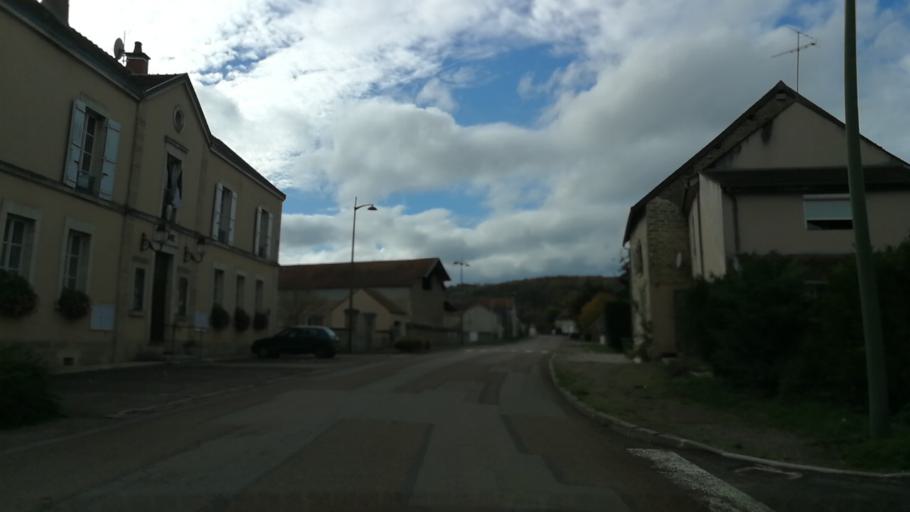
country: FR
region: Bourgogne
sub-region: Departement de la Cote-d'Or
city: Pouilly-en-Auxois
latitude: 47.2717
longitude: 4.4851
